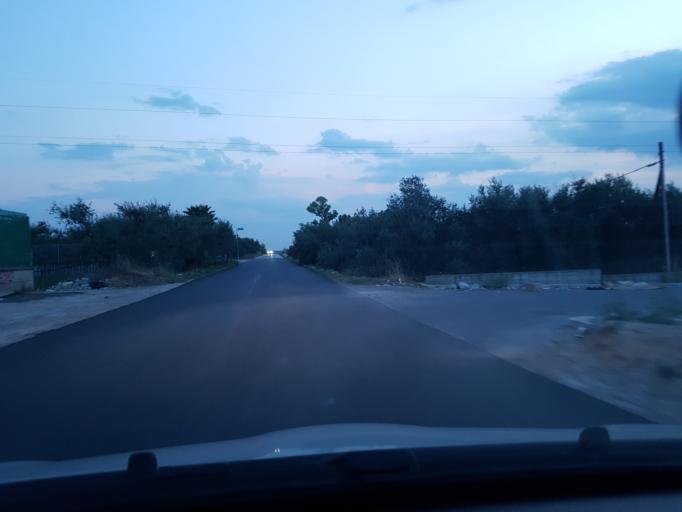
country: IT
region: Apulia
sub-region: Provincia di Foggia
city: Cerignola
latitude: 41.2590
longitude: 15.8813
